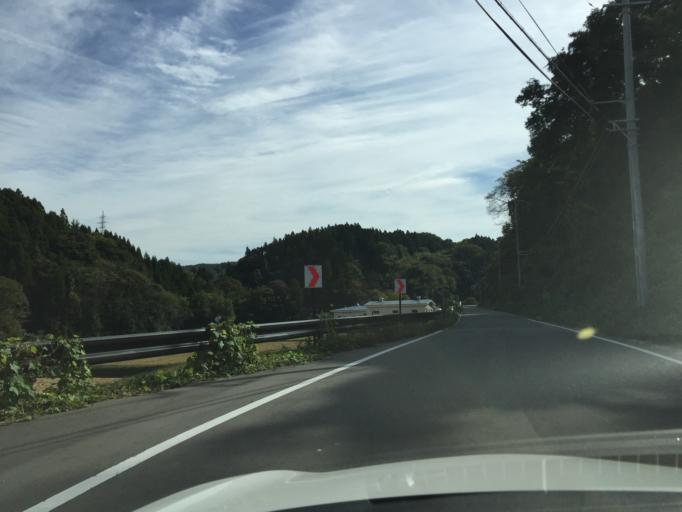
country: JP
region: Fukushima
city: Miharu
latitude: 37.5225
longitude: 140.5048
